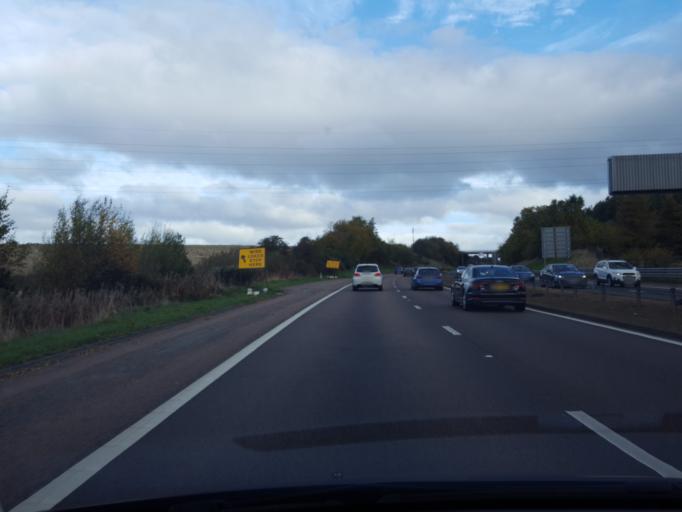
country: GB
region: Scotland
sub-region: Fife
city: Crossgates
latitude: 56.0916
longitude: -3.4015
